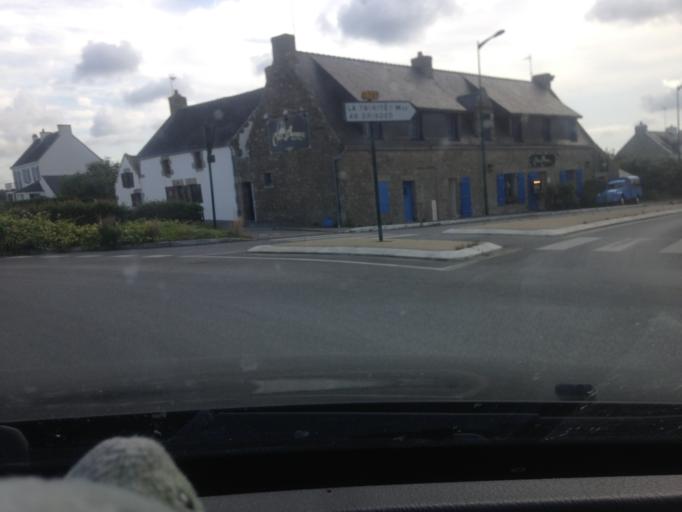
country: FR
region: Brittany
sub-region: Departement du Morbihan
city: Carnac
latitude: 47.5865
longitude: -3.0595
